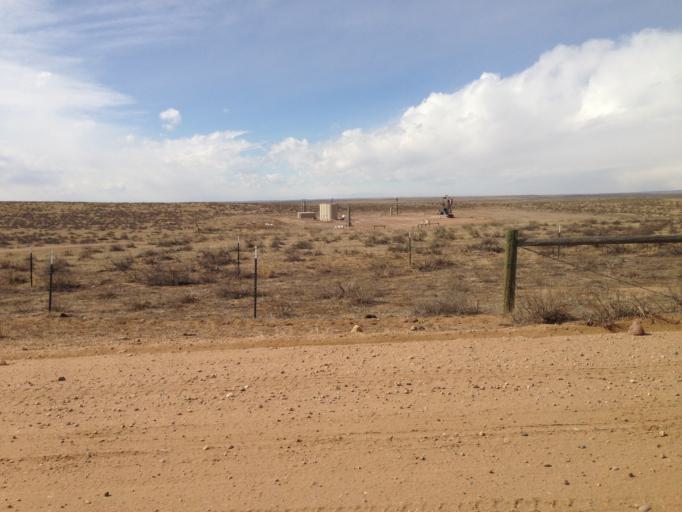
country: US
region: Colorado
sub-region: Weld County
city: Keenesburg
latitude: 40.2306
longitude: -104.2065
